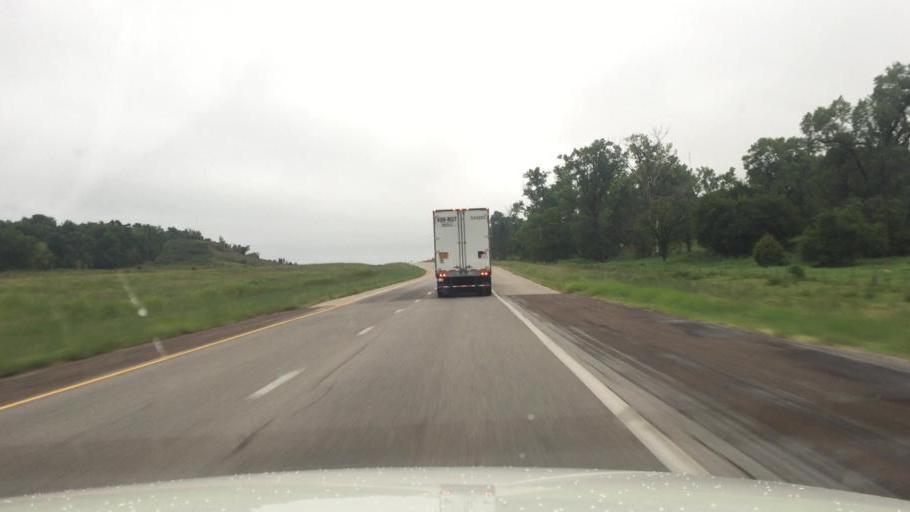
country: US
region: Kansas
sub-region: Montgomery County
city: Cherryvale
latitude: 37.2195
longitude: -95.5857
